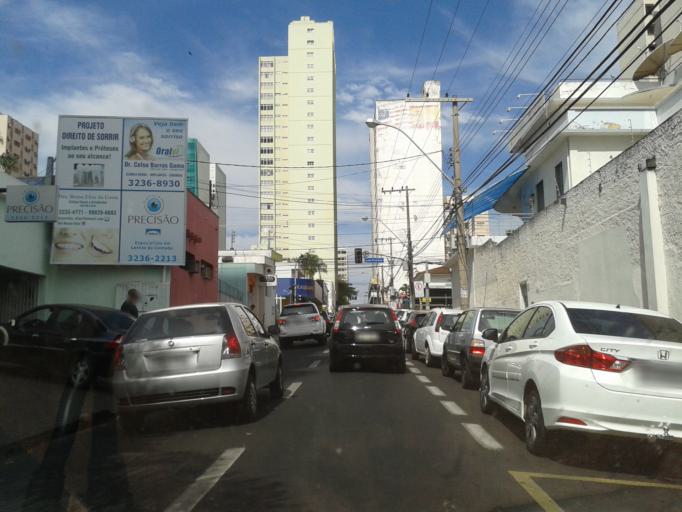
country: BR
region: Minas Gerais
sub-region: Uberlandia
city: Uberlandia
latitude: -18.9193
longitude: -48.2809
